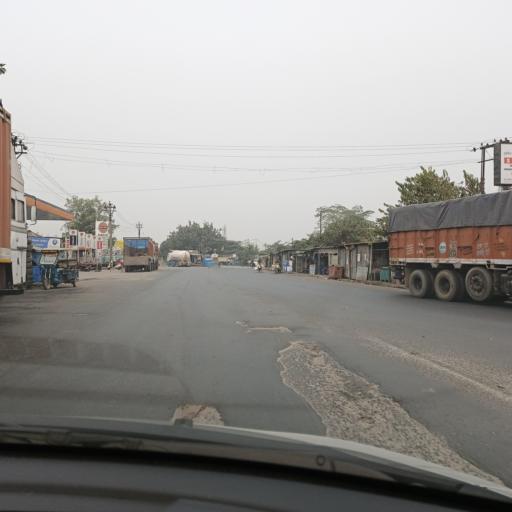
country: IN
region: West Bengal
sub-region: Darjiling
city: Shiliguri
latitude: 26.6571
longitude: 88.4157
